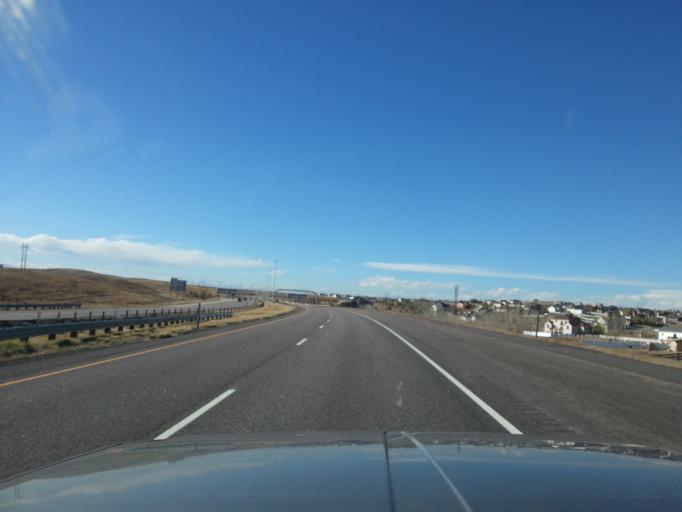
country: US
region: Colorado
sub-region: Adams County
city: Todd Creek
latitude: 39.9520
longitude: -104.8667
